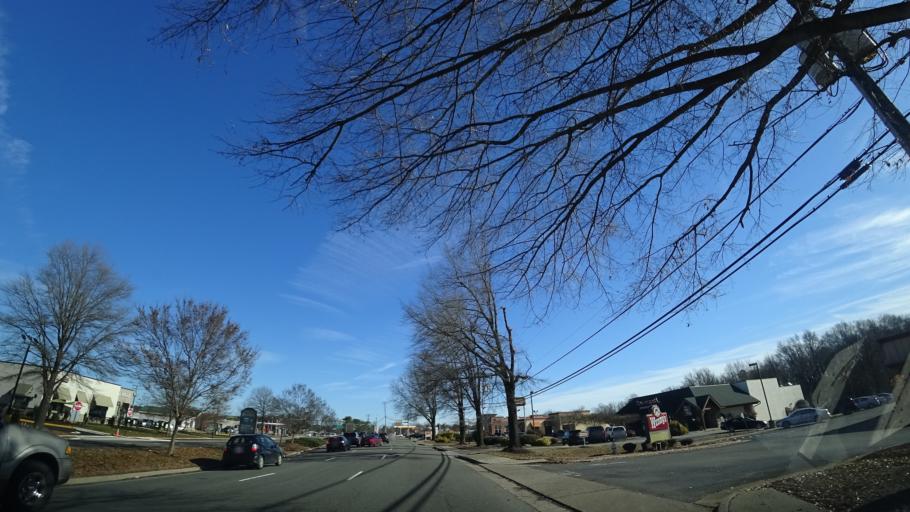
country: US
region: Virginia
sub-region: Hanover County
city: Ashland
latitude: 37.7581
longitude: -77.4660
